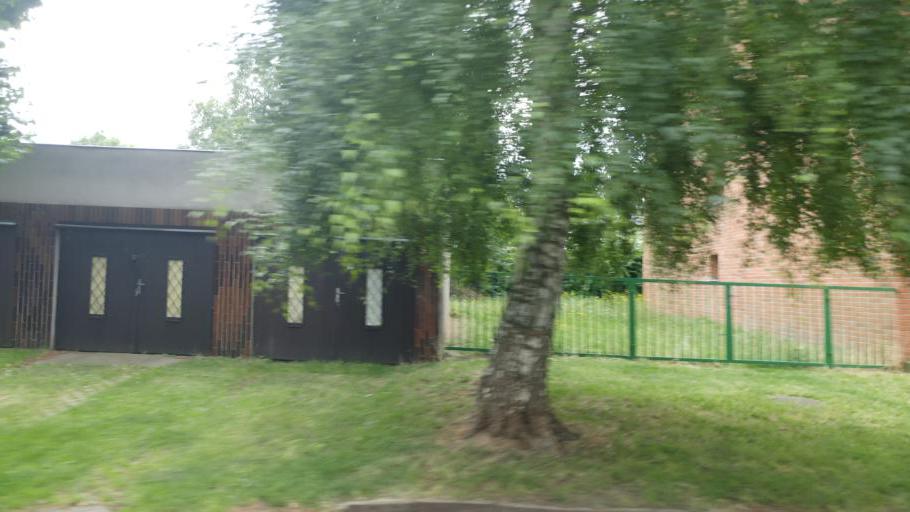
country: CZ
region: Central Bohemia
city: Horomerice
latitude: 50.1324
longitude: 14.3715
